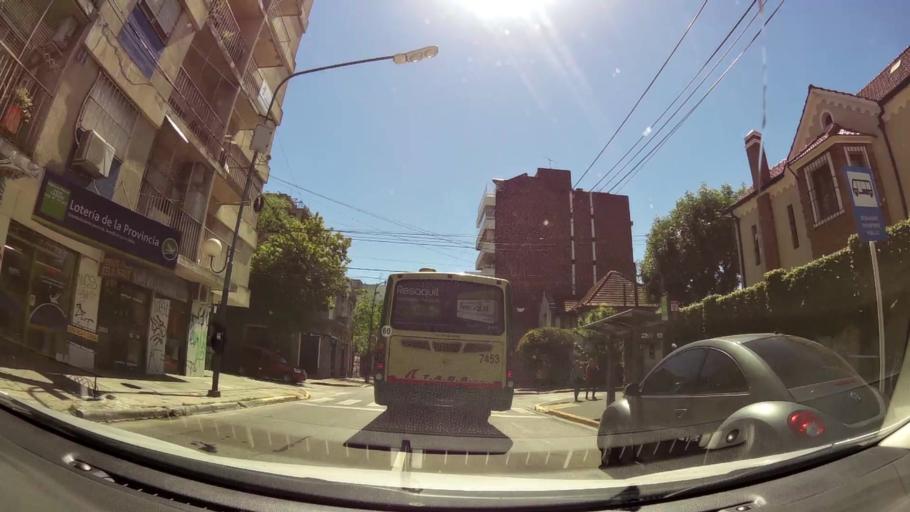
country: AR
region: Buenos Aires
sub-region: Partido de Vicente Lopez
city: Olivos
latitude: -34.5317
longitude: -58.4997
